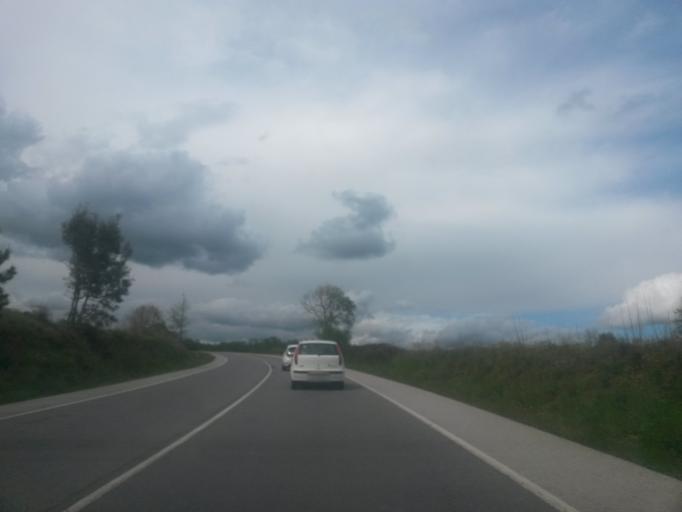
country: ES
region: Catalonia
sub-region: Provincia de Girona
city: Brunyola
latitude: 41.9112
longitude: 2.6597
